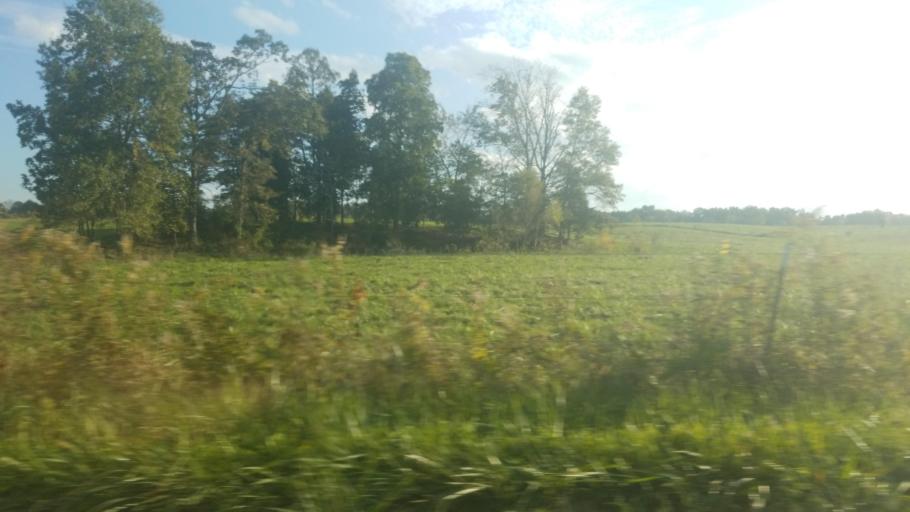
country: US
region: Illinois
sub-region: Saline County
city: Carrier Mills
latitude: 37.8038
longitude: -88.7074
